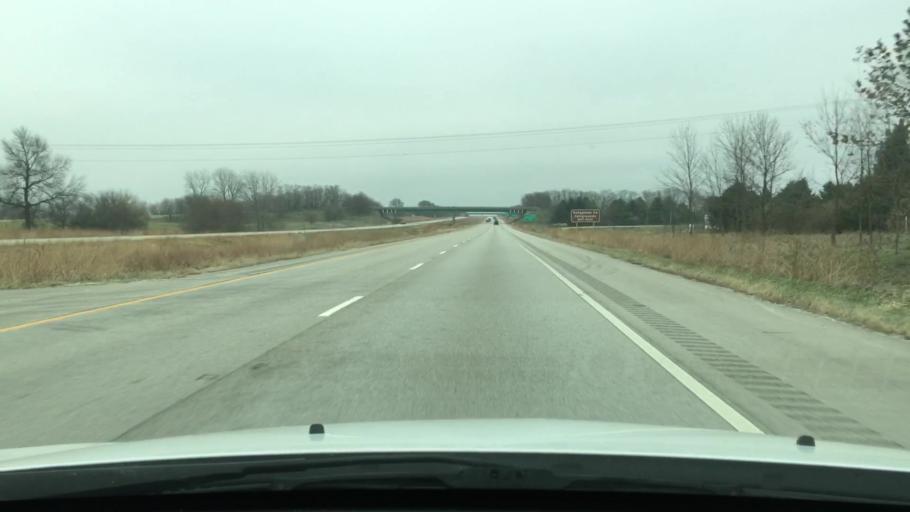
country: US
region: Illinois
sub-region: Sangamon County
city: New Berlin
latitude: 39.7399
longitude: -89.9431
